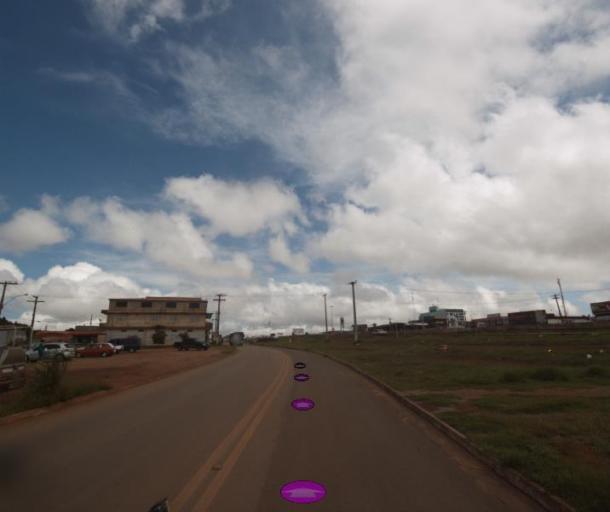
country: BR
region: Federal District
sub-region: Brasilia
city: Brasilia
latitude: -15.7360
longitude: -48.2814
